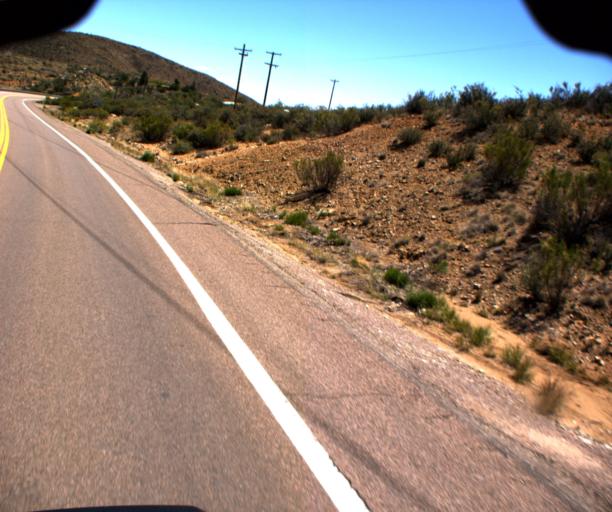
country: US
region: Arizona
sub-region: Yavapai County
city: Bagdad
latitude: 34.5652
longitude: -113.1730
